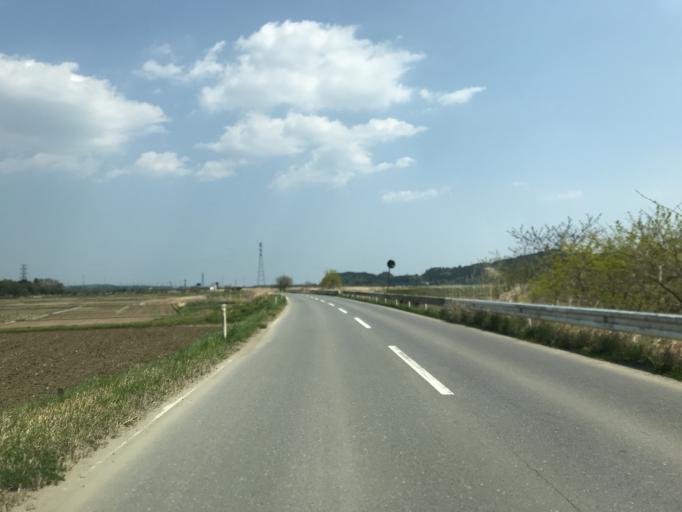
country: JP
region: Ibaraki
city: Kitaibaraki
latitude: 36.9250
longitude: 140.7449
